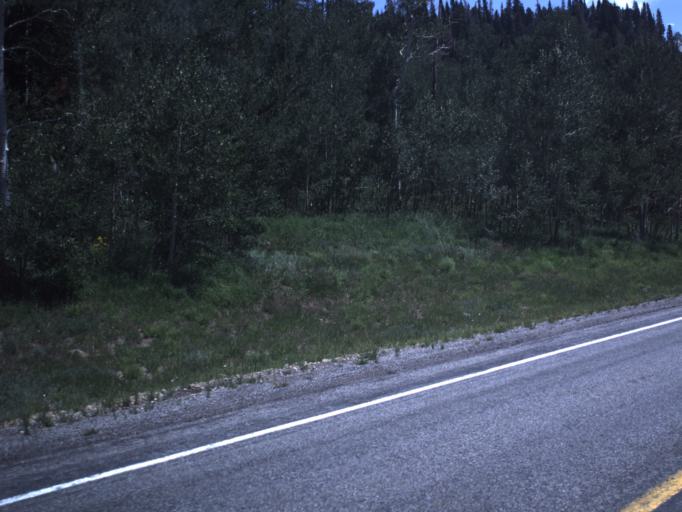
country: US
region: Utah
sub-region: Sanpete County
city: Fairview
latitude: 39.6052
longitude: -111.2761
